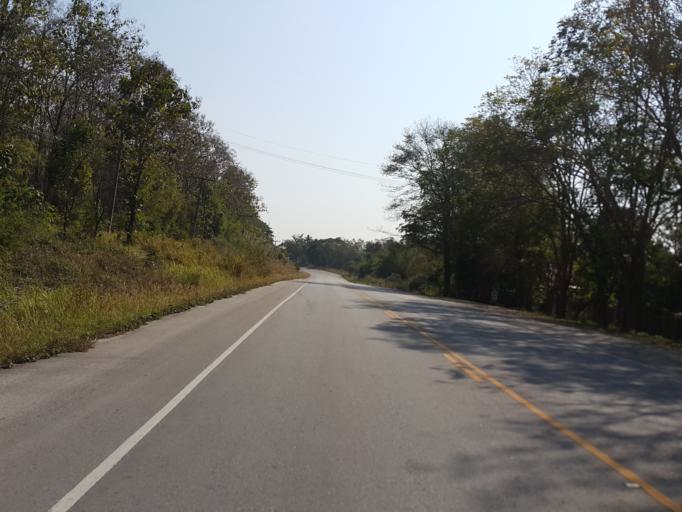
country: TH
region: Lampang
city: Mueang Pan
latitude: 18.8029
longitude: 99.5873
